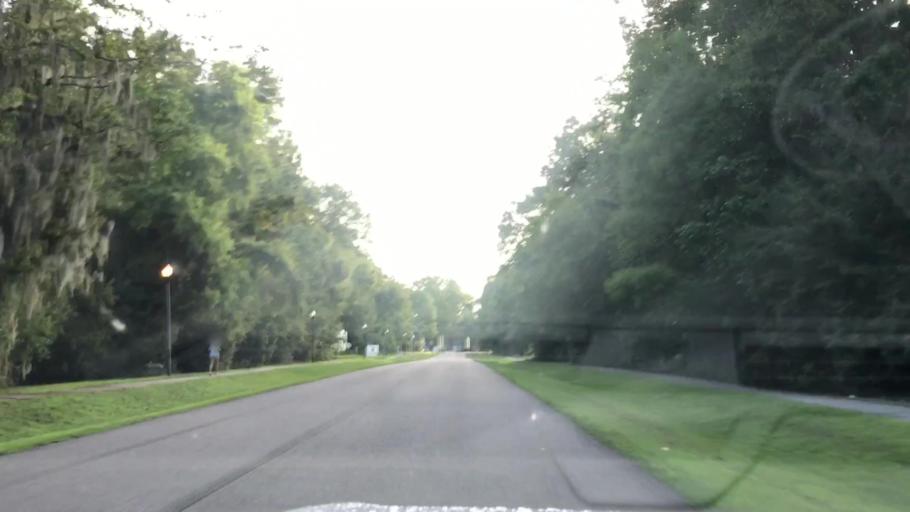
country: US
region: South Carolina
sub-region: Charleston County
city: Shell Point
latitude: 32.8399
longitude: -80.0932
